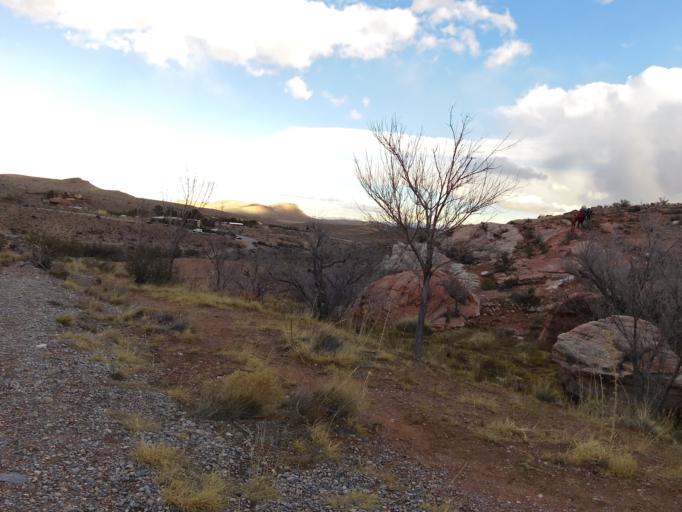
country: US
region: Nevada
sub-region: Clark County
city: Summerlin South
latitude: 36.1503
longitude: -115.4235
